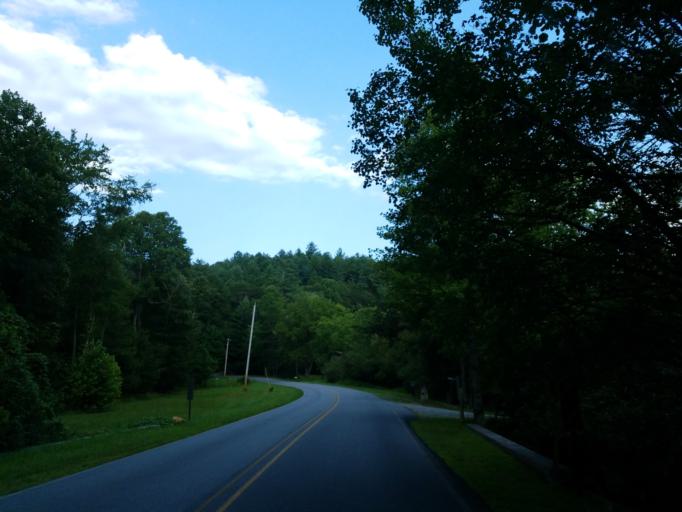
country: US
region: Georgia
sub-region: Fannin County
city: Blue Ridge
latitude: 34.7783
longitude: -84.2716
